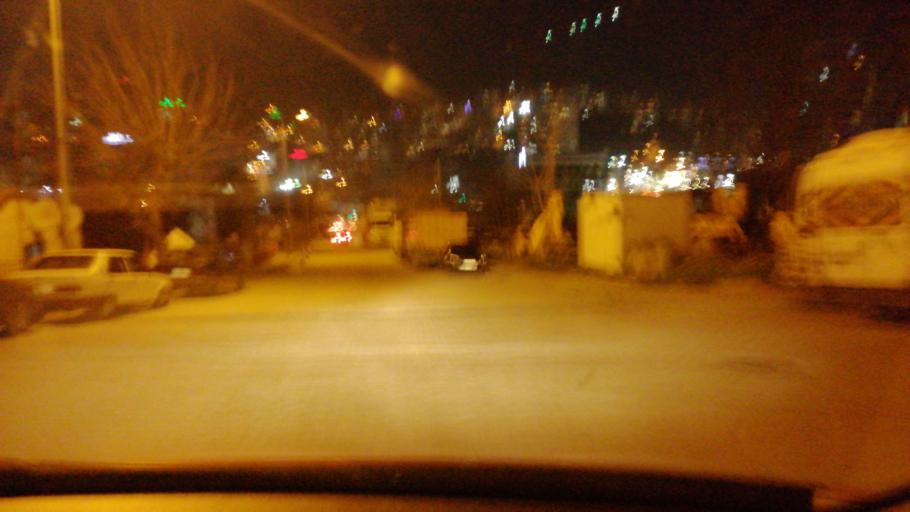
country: TR
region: Istanbul
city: Sisli
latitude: 41.0807
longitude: 28.9780
